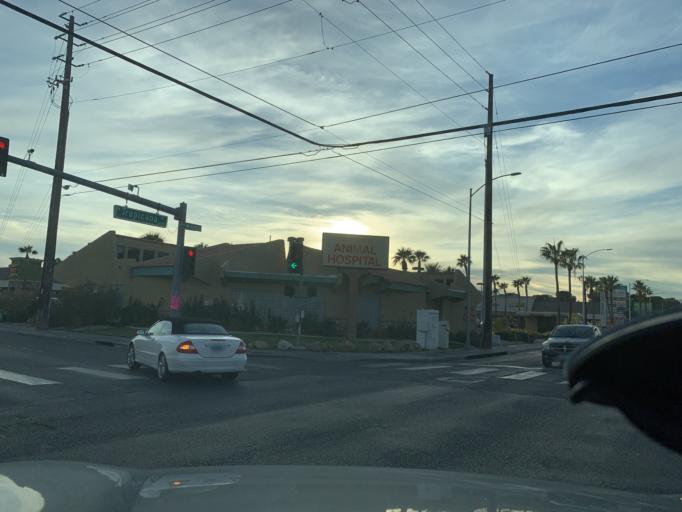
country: US
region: Nevada
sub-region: Clark County
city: Spring Valley
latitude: 36.0999
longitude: -115.2251
